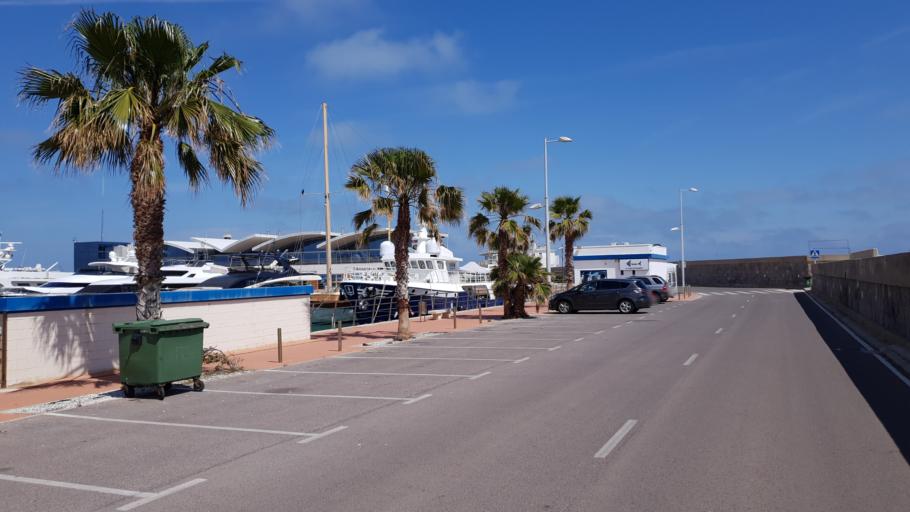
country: ES
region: Valencia
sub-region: Provincia de Castello
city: Burriana
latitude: 39.8592
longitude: -0.0711
